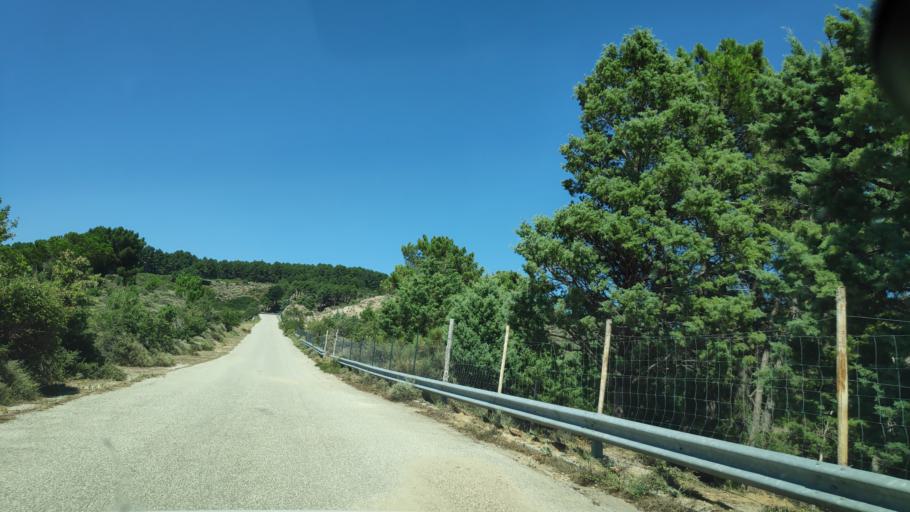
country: IT
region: Calabria
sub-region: Provincia di Reggio Calabria
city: Bova
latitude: 38.0229
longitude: 15.9397
